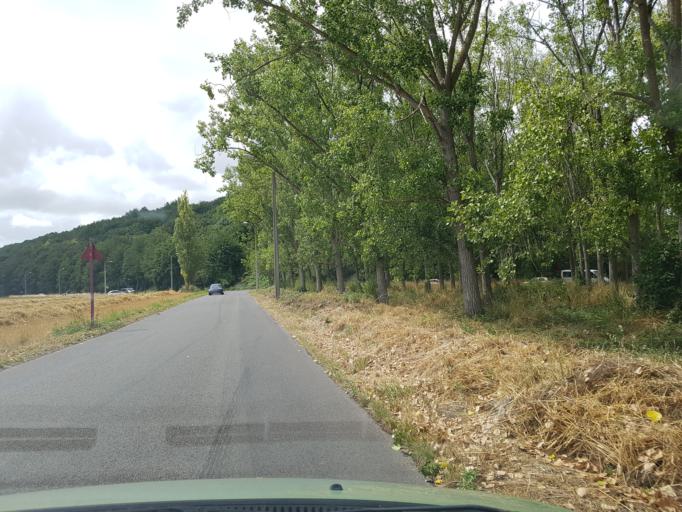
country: FR
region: Nord-Pas-de-Calais
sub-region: Departement du Pas-de-Calais
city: Grenay
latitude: 50.4650
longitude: 2.7453
